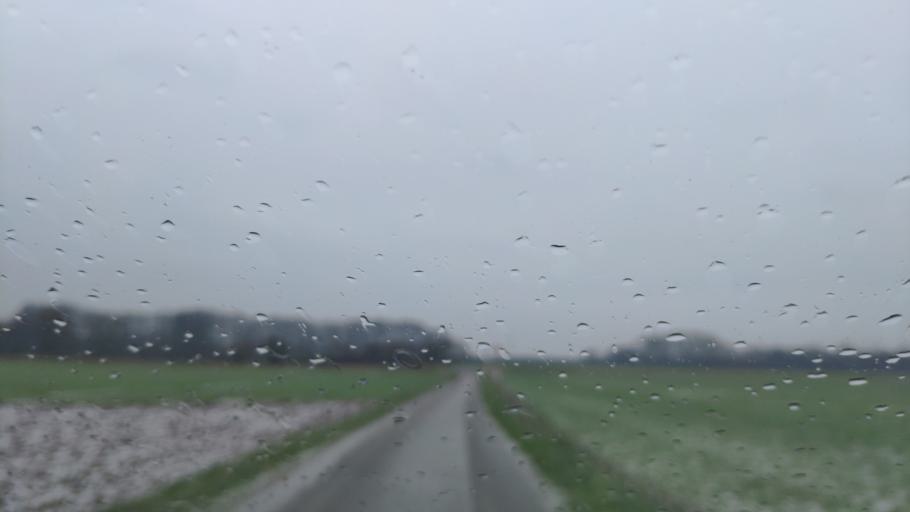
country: FR
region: Haute-Normandie
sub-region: Departement de la Seine-Maritime
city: Neville
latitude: 49.7938
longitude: 0.6925
